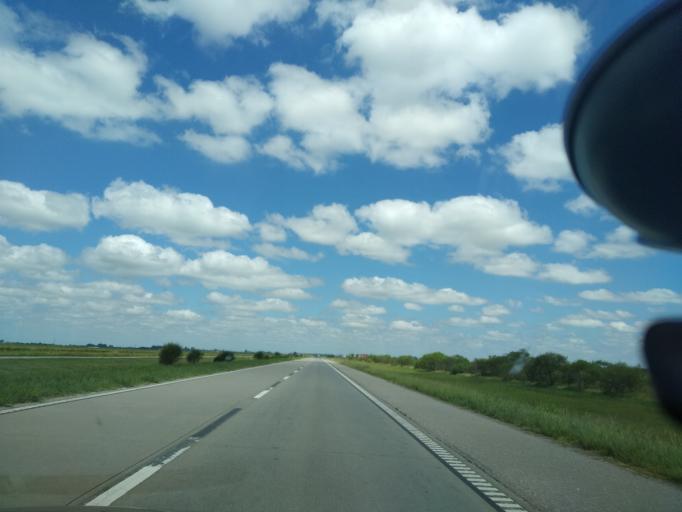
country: AR
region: Cordoba
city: Tio Pujio
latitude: -32.3182
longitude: -63.2746
